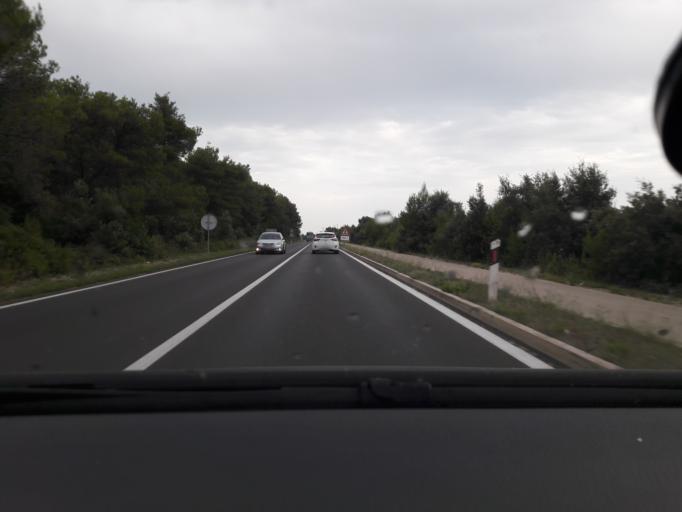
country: HR
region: Zadarska
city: Nin
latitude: 44.1955
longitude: 15.1773
